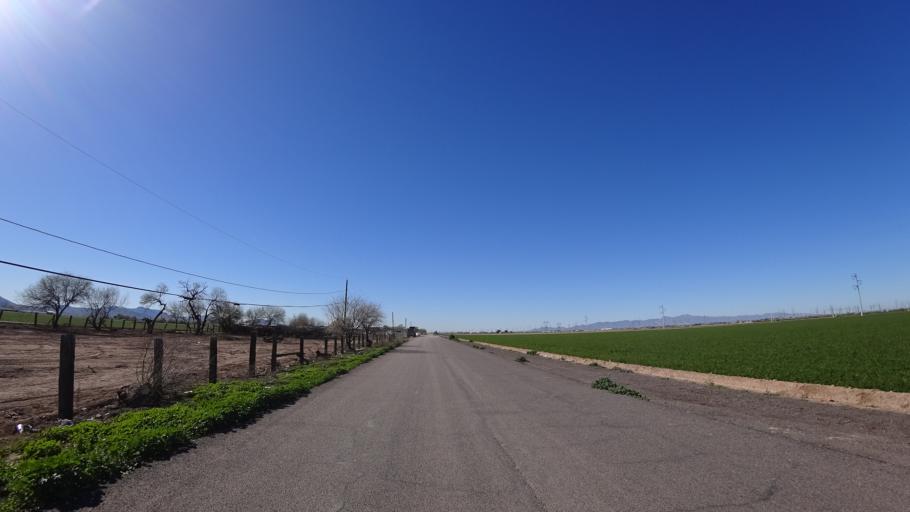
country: US
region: Arizona
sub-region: Maricopa County
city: Avondale
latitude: 33.3958
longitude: -112.3073
